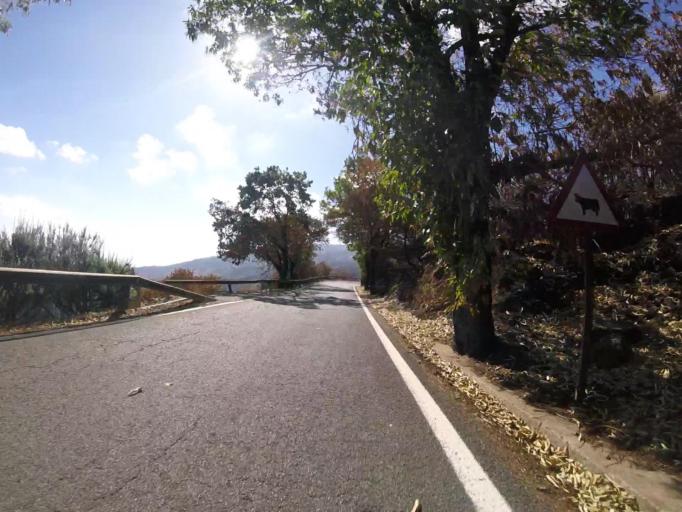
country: ES
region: Canary Islands
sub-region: Provincia de Las Palmas
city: Valleseco
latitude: 28.0105
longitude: -15.5844
